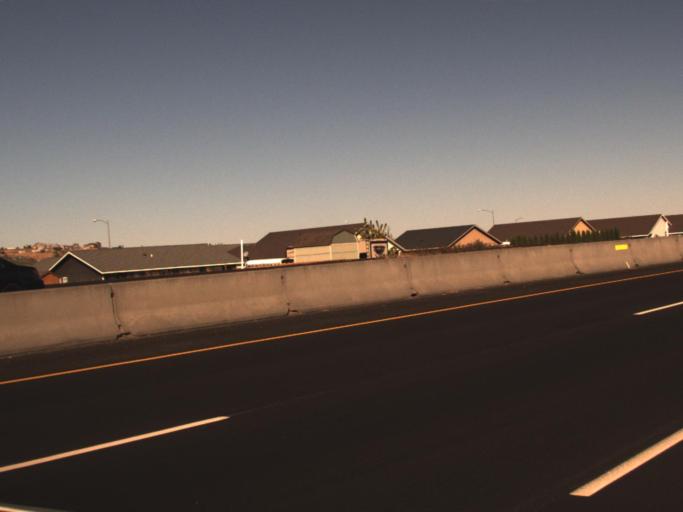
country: US
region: Washington
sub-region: Benton County
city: Richland
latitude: 46.2726
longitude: -119.3064
